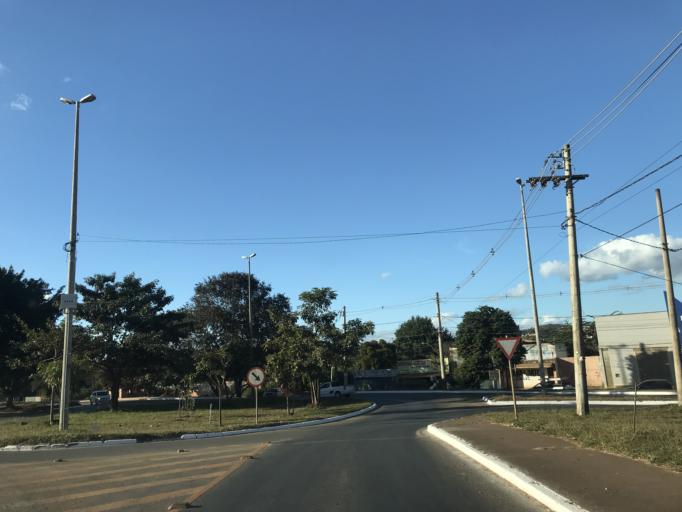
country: BR
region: Federal District
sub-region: Brasilia
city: Brasilia
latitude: -15.8886
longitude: -47.7801
